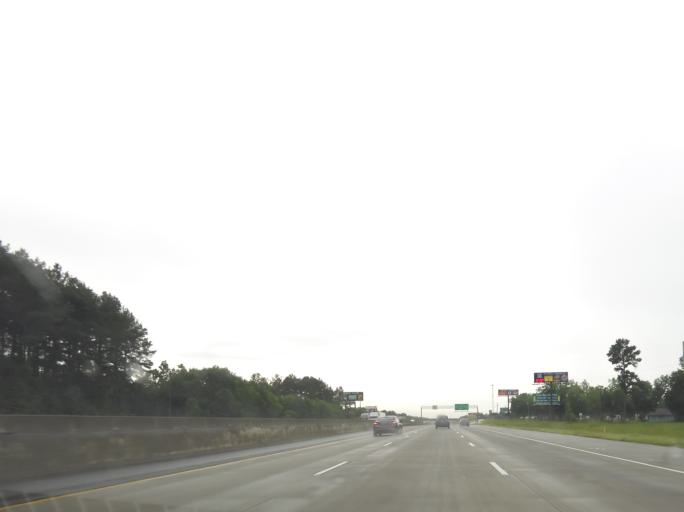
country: US
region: Georgia
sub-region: Lowndes County
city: Hahira
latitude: 31.0496
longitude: -83.3973
